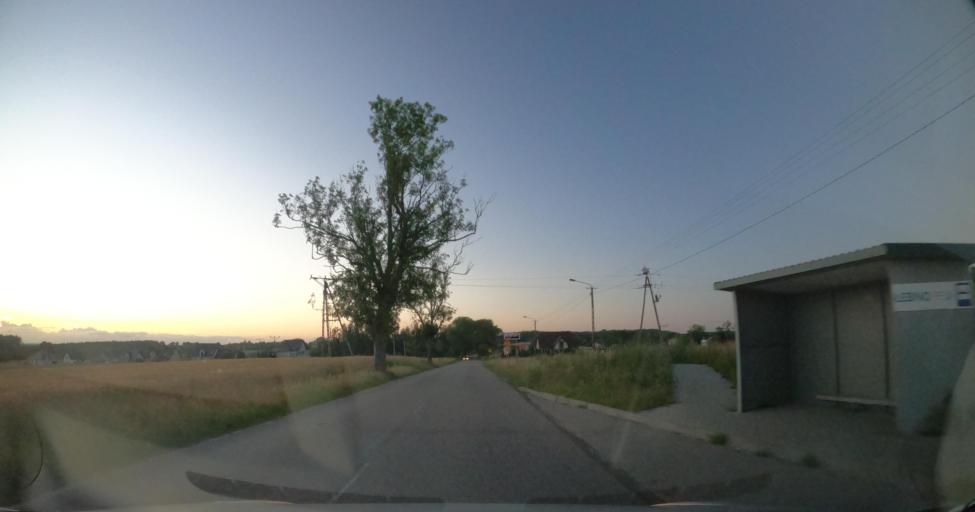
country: PL
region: Pomeranian Voivodeship
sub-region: Powiat wejherowski
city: Szemud
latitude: 54.4642
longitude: 18.1405
